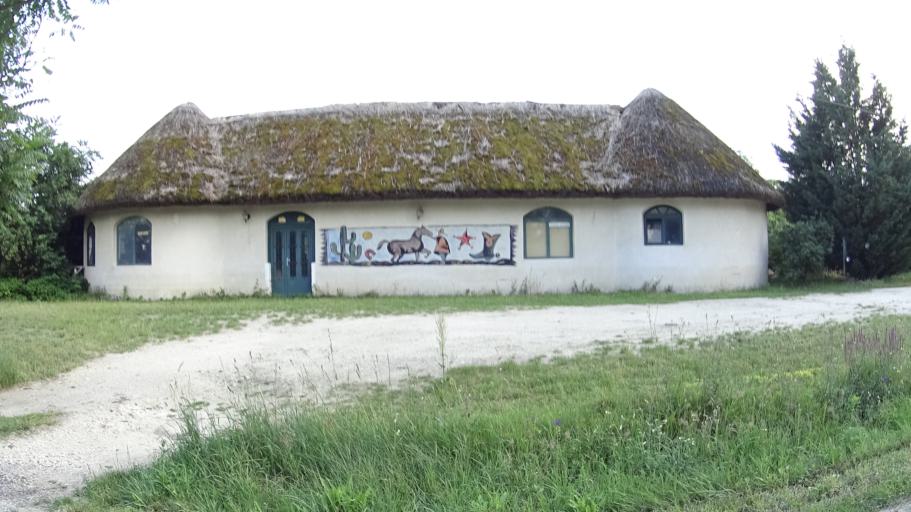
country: HU
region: Pest
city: Dunabogdany
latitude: 47.7996
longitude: 19.0458
